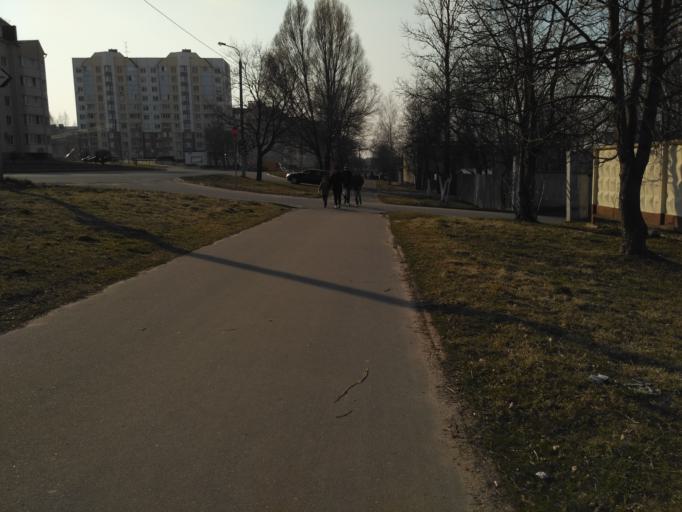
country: BY
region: Minsk
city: Zaslawye
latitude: 54.0129
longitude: 27.2633
